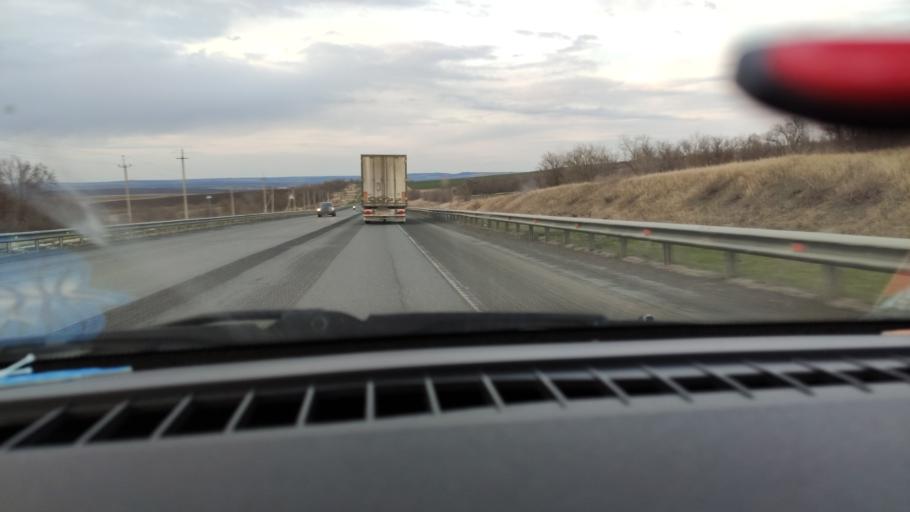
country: RU
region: Saratov
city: Shumeyka
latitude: 51.7830
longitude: 46.1303
